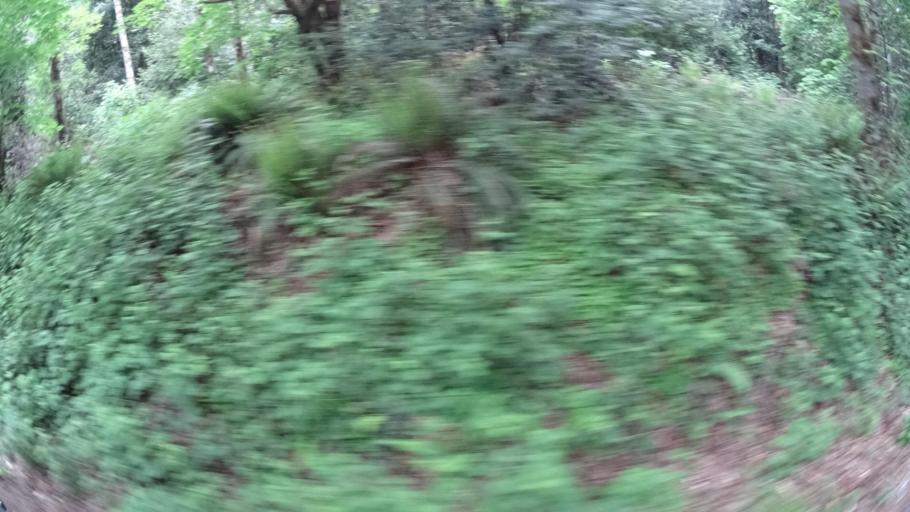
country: US
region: California
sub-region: Humboldt County
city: Willow Creek
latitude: 41.2030
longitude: -123.7559
